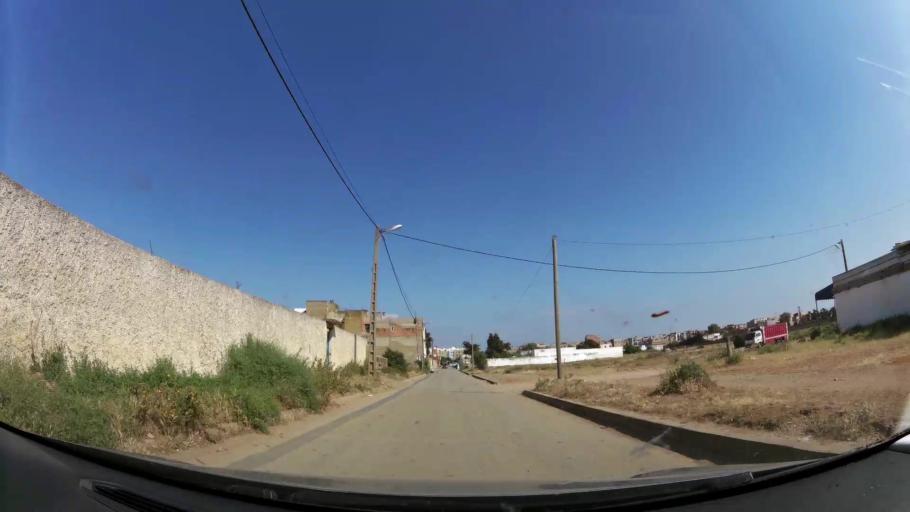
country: MA
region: Rabat-Sale-Zemmour-Zaer
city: Sale
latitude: 34.0723
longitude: -6.7604
